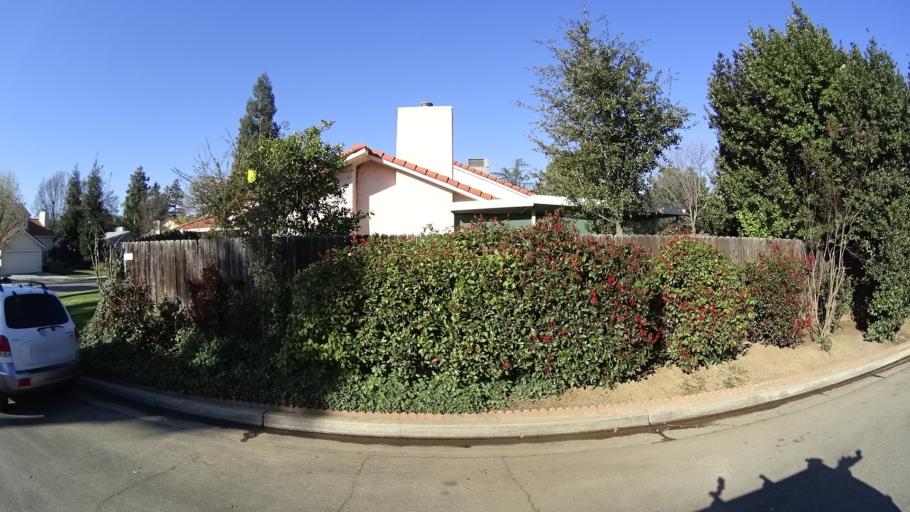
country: US
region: California
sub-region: Fresno County
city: Clovis
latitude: 36.8729
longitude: -119.7527
